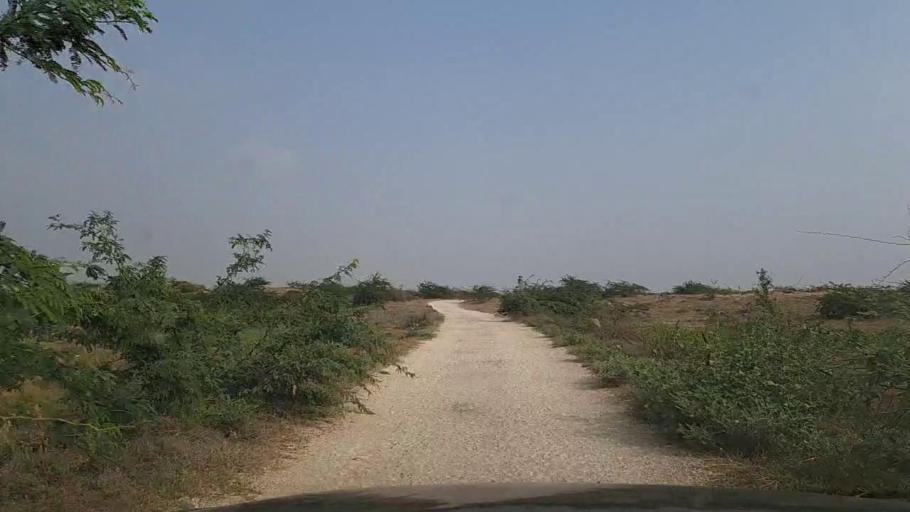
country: PK
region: Sindh
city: Thatta
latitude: 24.8595
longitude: 67.7793
